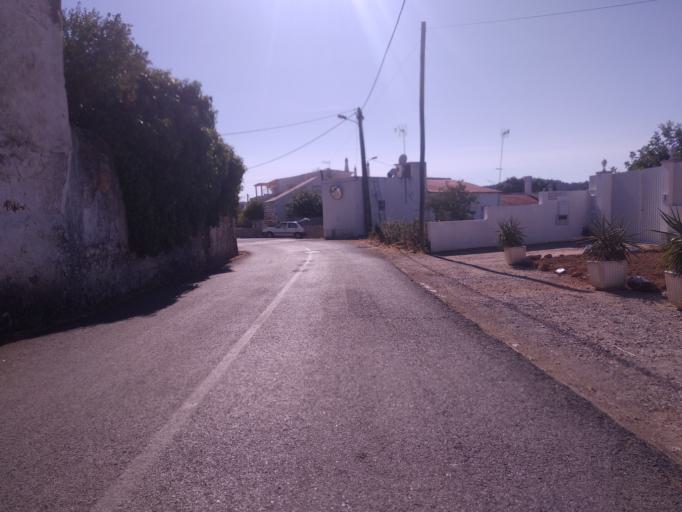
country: PT
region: Faro
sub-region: Sao Bras de Alportel
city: Sao Bras de Alportel
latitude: 37.1703
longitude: -7.8939
